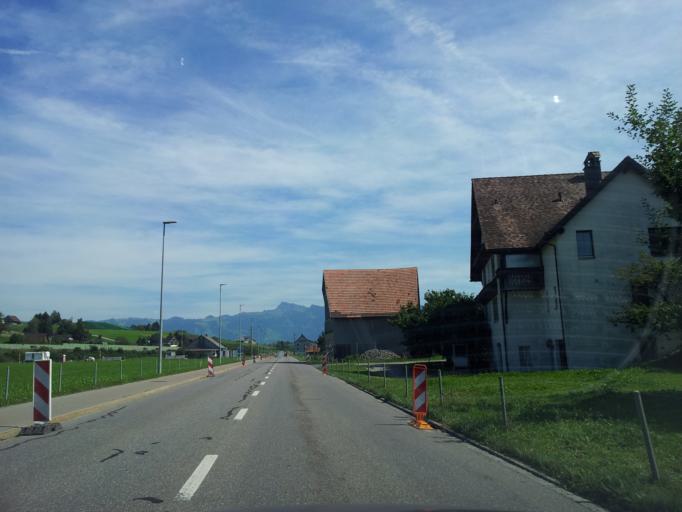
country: CH
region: Schwyz
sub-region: Bezirk March
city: Schubelbach
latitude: 47.1913
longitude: 8.8971
